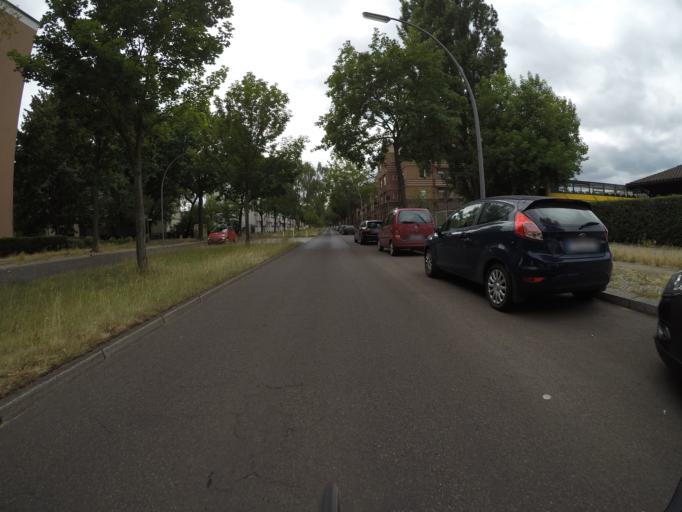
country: DE
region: Berlin
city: Reinickendorf
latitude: 52.5608
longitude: 13.3405
